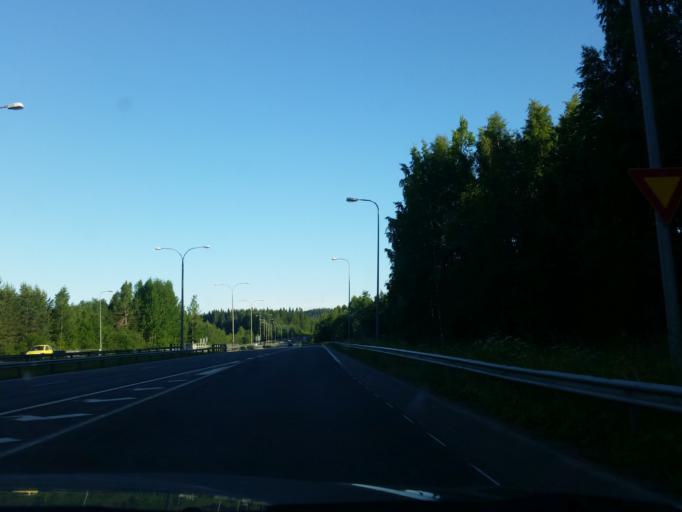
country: FI
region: Northern Savo
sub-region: Kuopio
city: Kuopio
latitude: 62.8601
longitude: 27.6185
